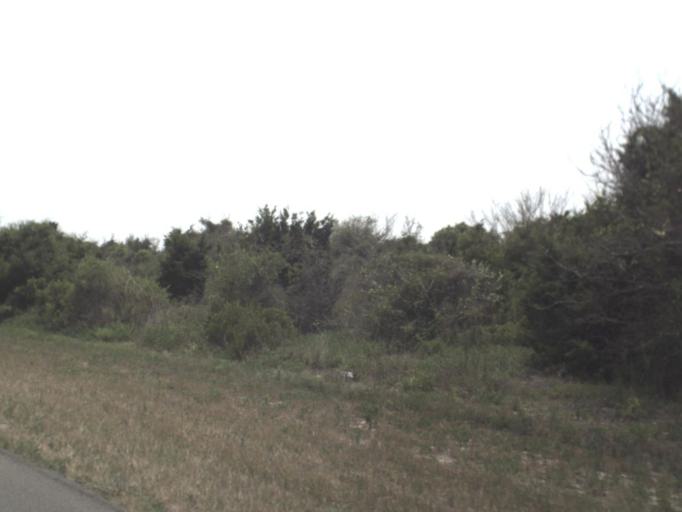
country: US
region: Florida
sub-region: Duval County
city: Atlantic Beach
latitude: 30.4370
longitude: -81.4145
